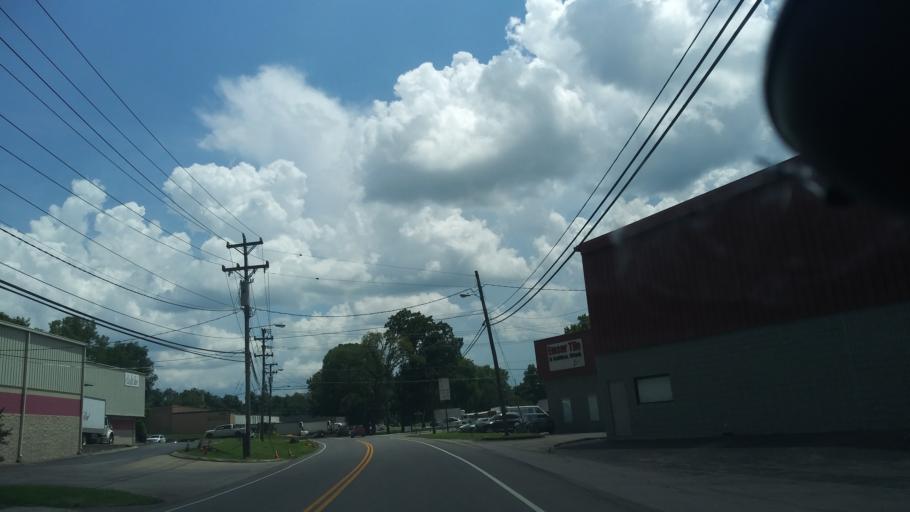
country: US
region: Tennessee
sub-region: Davidson County
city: Oak Hill
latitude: 36.1243
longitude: -86.7659
